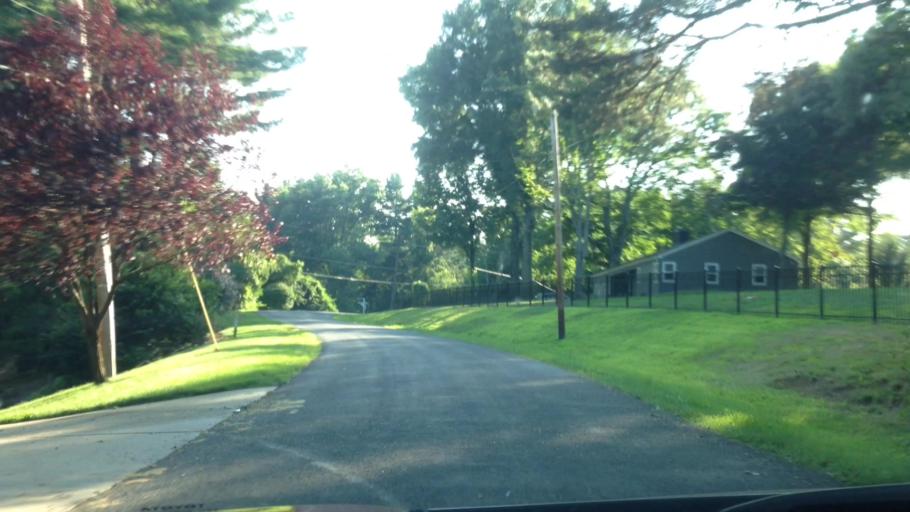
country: US
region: Ohio
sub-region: Summit County
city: Montrose-Ghent
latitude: 41.1609
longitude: -81.6342
